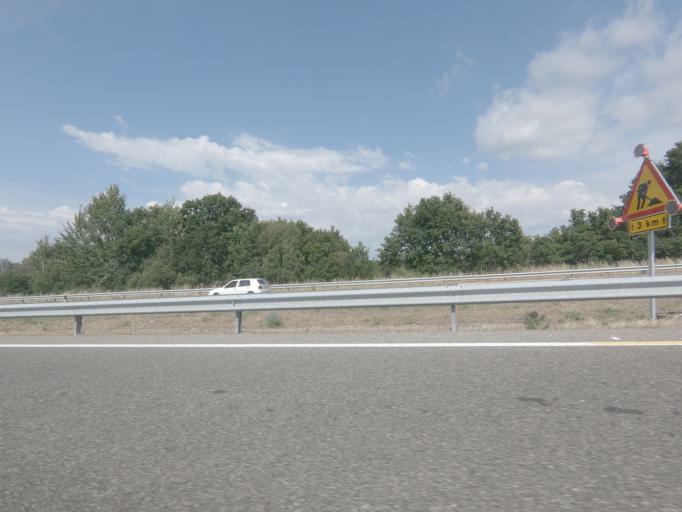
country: ES
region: Galicia
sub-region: Provincia de Ourense
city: Taboadela
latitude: 42.2621
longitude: -7.8684
